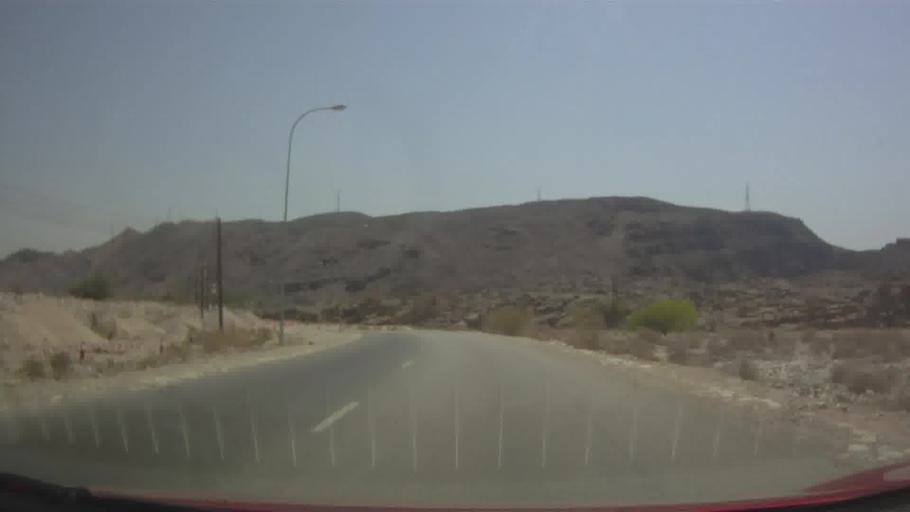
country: OM
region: Muhafazat Masqat
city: Muscat
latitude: 23.5111
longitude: 58.6354
